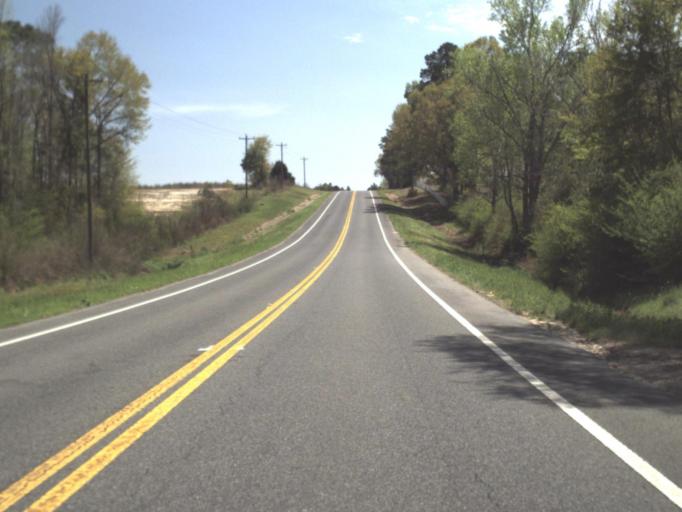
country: US
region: Alabama
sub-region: Geneva County
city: Geneva
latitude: 30.8861
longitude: -85.9509
